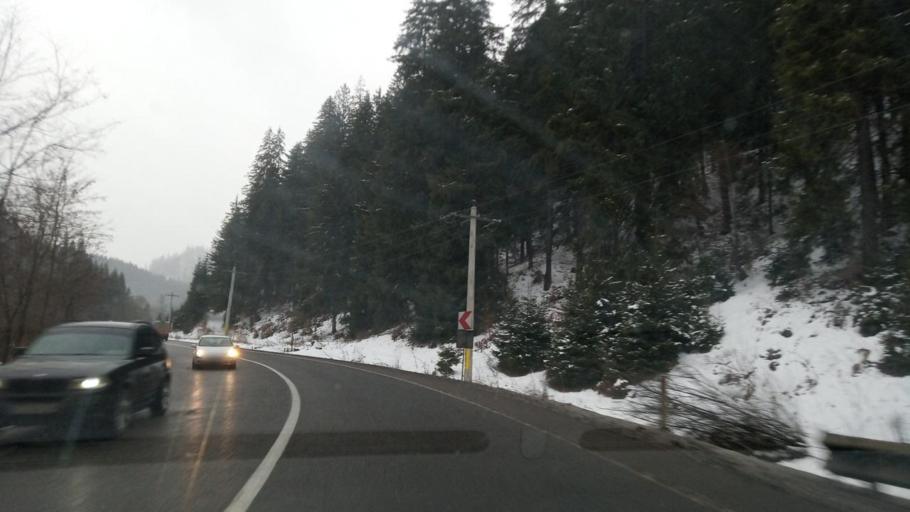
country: RO
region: Suceava
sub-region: Comuna Fundu Moldovei
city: Fundu Moldovei
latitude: 47.5079
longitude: 25.4191
